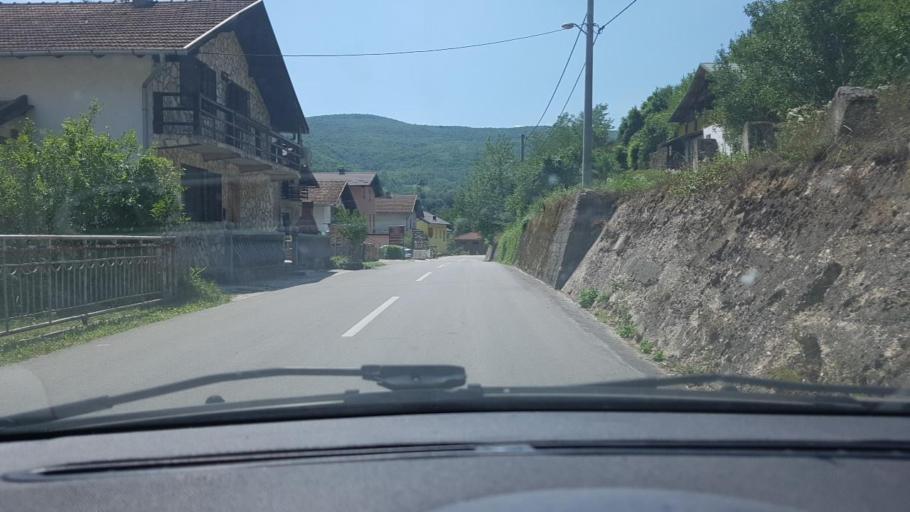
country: BA
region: Federation of Bosnia and Herzegovina
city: Orasac
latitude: 44.5650
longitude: 16.0912
